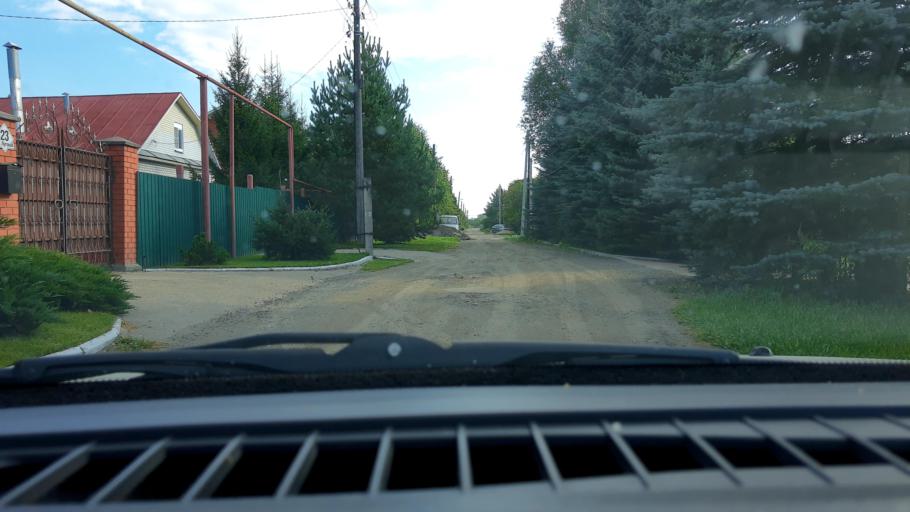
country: RU
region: Nizjnij Novgorod
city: Burevestnik
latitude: 56.1647
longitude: 43.7324
